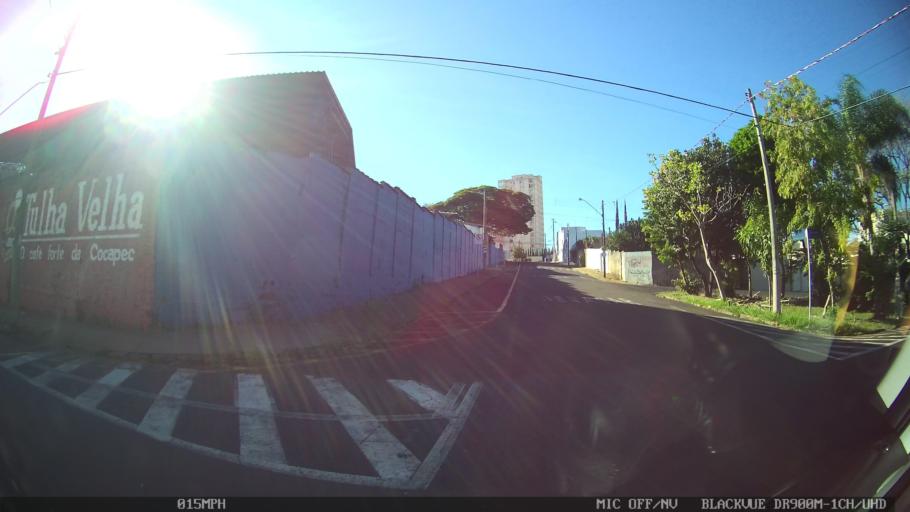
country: BR
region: Sao Paulo
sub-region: Franca
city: Franca
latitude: -20.5468
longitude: -47.4078
